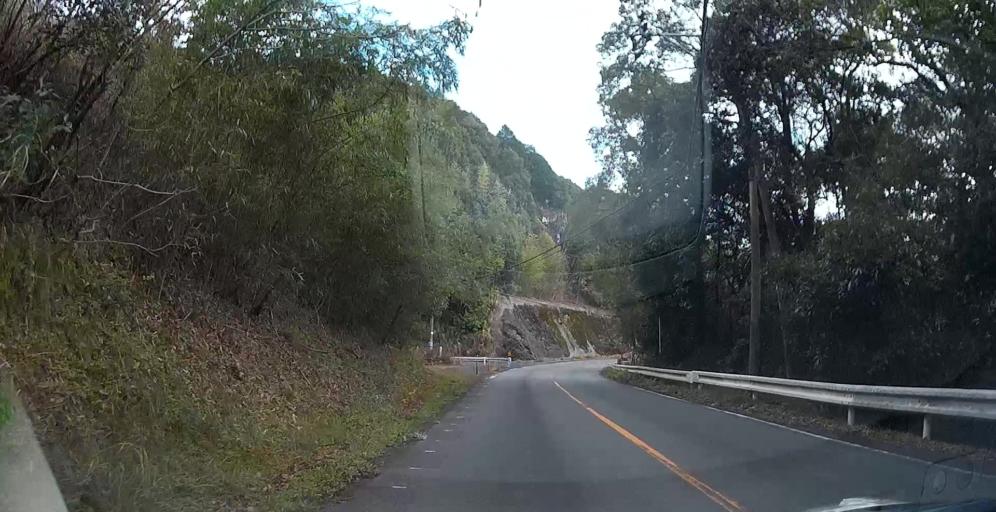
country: JP
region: Kumamoto
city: Yatsushiro
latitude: 32.3684
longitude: 130.5056
